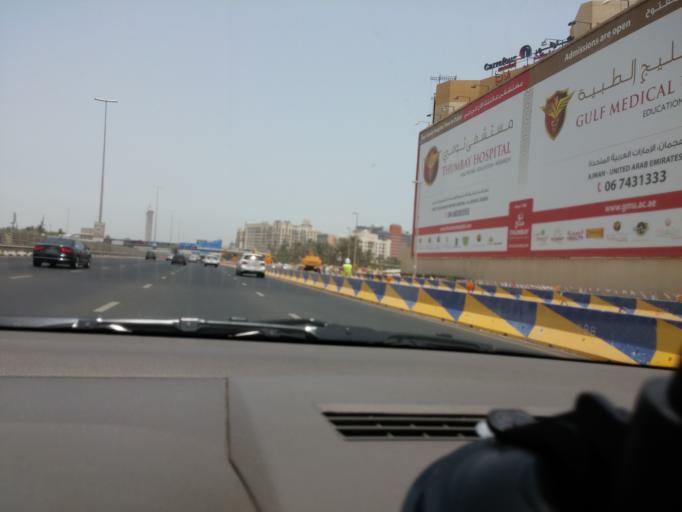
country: AE
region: Ash Shariqah
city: Sharjah
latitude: 25.2277
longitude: 55.3190
